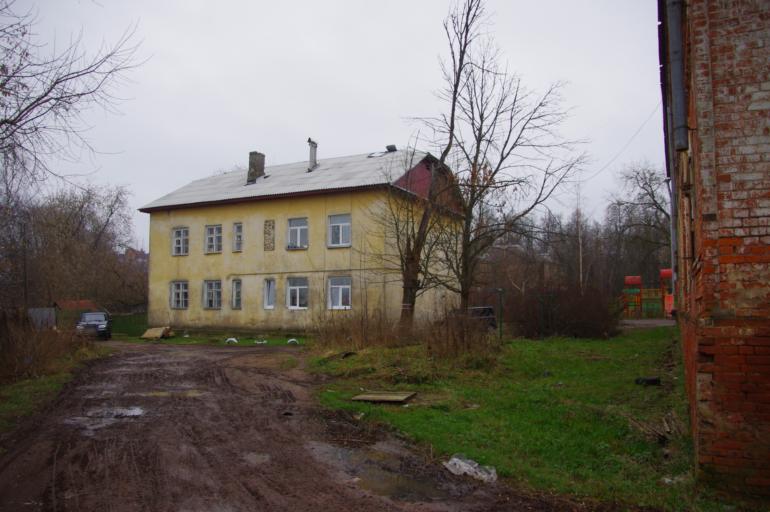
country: RU
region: Moskovskaya
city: Opalikha
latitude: 55.8439
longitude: 37.2541
